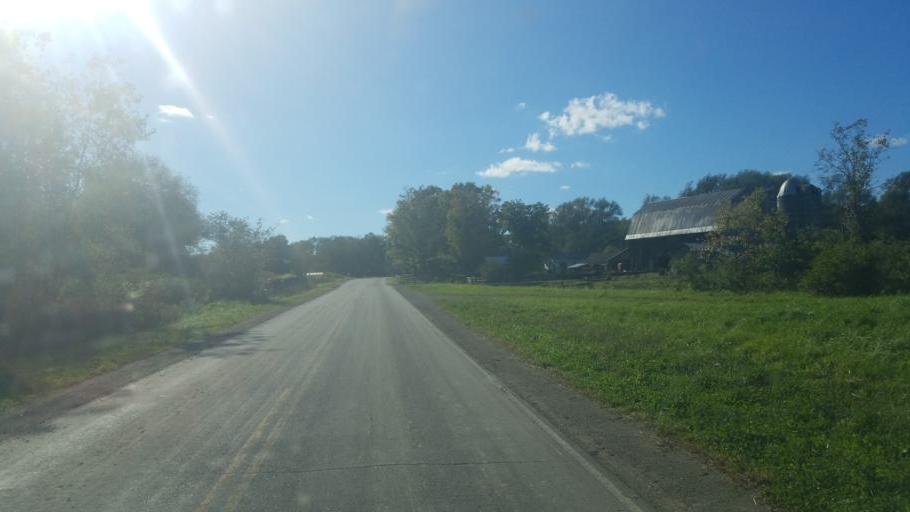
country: US
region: New York
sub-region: Allegany County
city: Cuba
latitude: 42.2762
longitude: -78.2183
